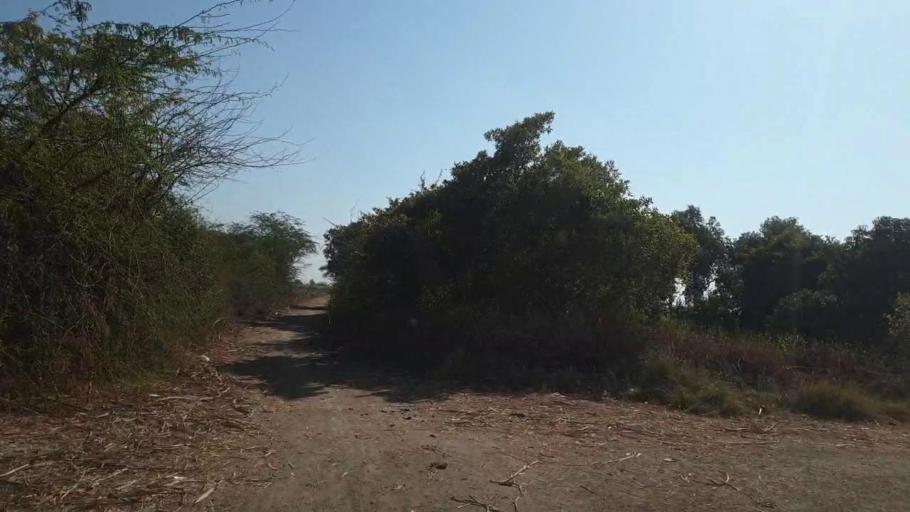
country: PK
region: Sindh
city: Mirpur Khas
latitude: 25.6433
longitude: 69.0227
